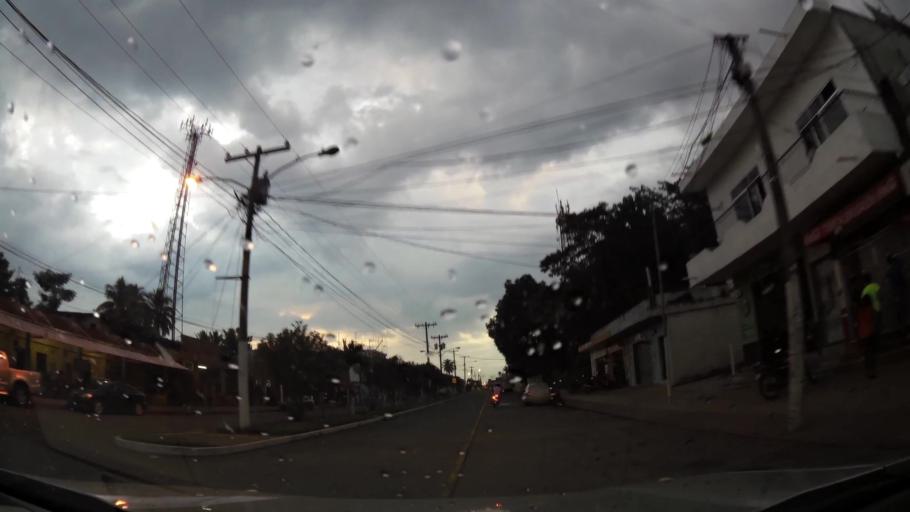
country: GT
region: Escuintla
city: Santa Lucia Cotzumalguapa
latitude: 14.3304
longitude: -91.0195
